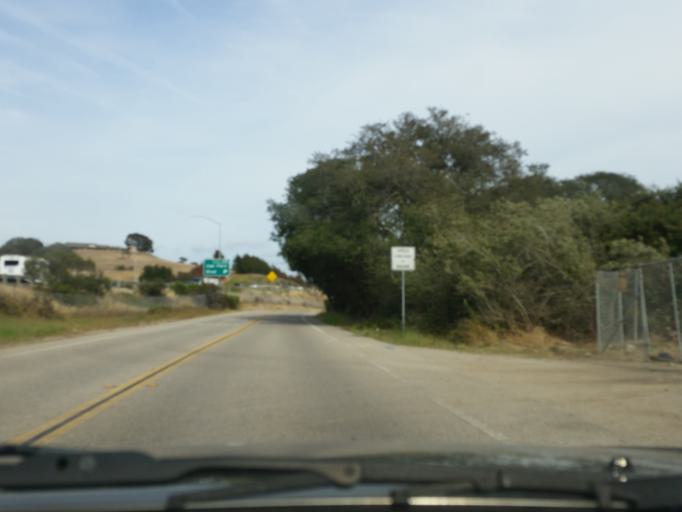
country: US
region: California
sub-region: San Luis Obispo County
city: Grover Beach
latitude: 35.1339
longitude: -120.6182
